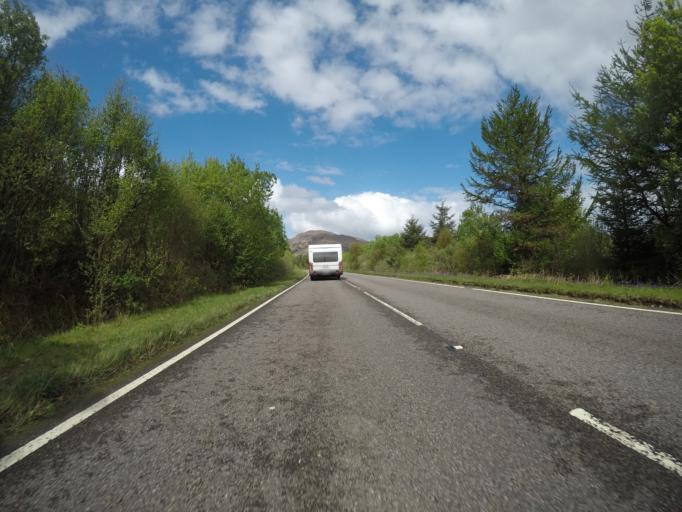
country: GB
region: Scotland
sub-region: Highland
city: Portree
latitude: 57.2588
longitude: -5.9421
